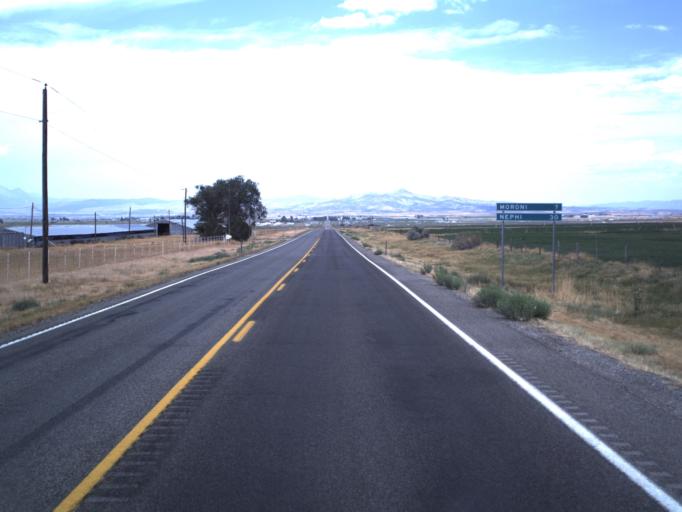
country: US
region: Utah
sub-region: Sanpete County
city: Ephraim
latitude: 39.4253
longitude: -111.5622
